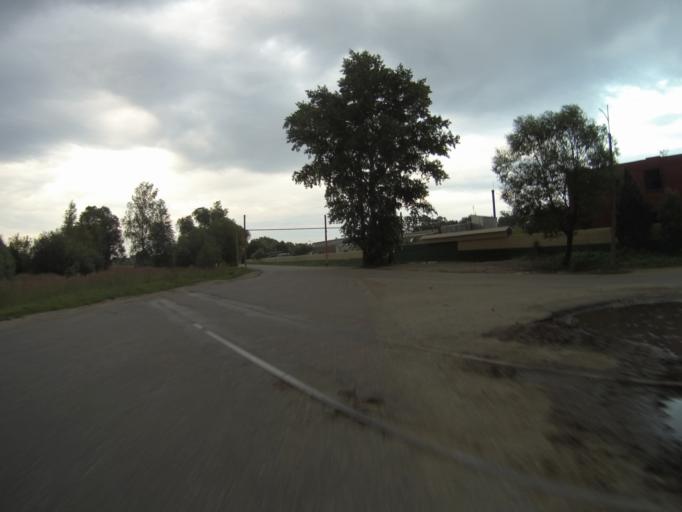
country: RU
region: Vladimir
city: Kameshkovo
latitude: 56.3465
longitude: 40.9778
